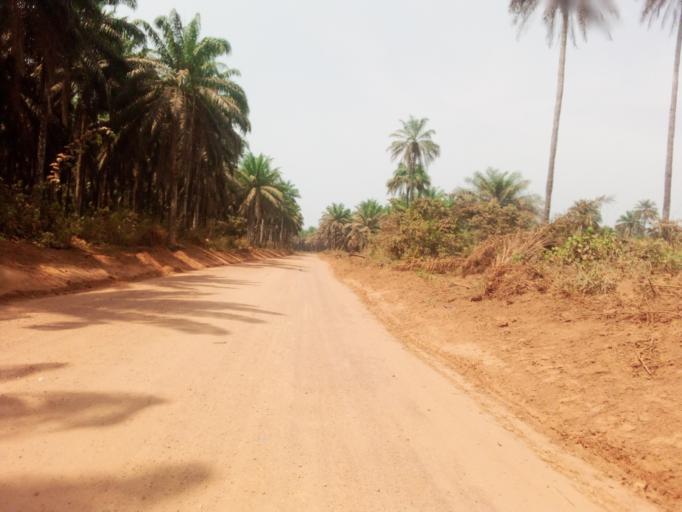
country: SL
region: Southern Province
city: Sumbuya
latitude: 7.6200
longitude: -12.1209
